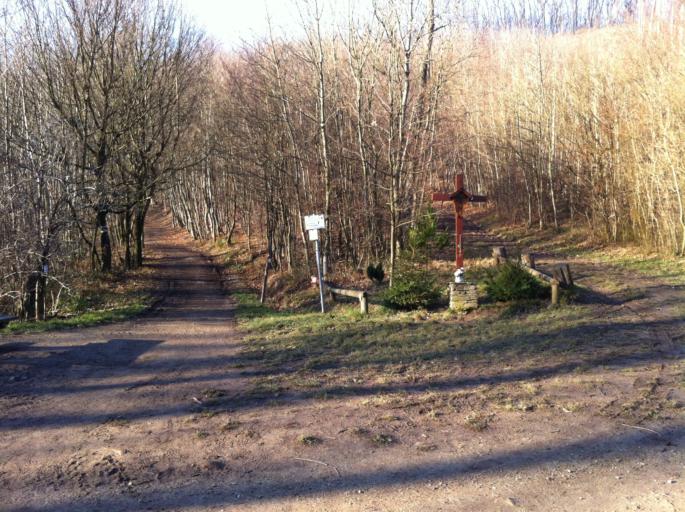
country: AT
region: Lower Austria
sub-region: Politischer Bezirk Wien-Umgebung
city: Klosterneuburg
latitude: 48.2708
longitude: 16.3130
